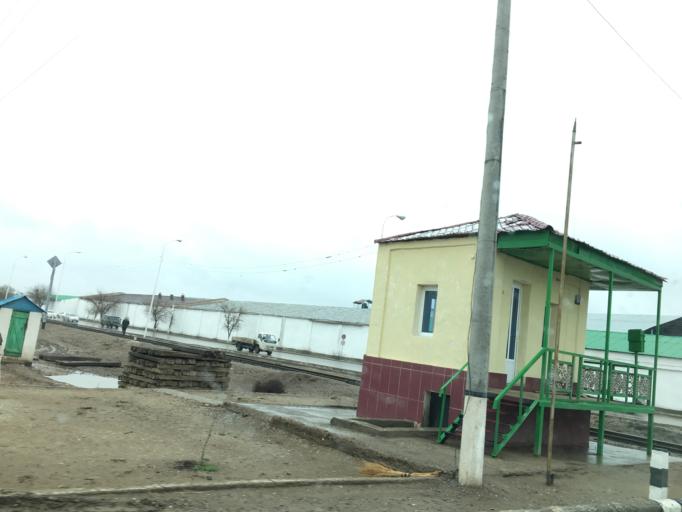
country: TM
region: Mary
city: Yoloeten
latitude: 37.2888
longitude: 62.3600
